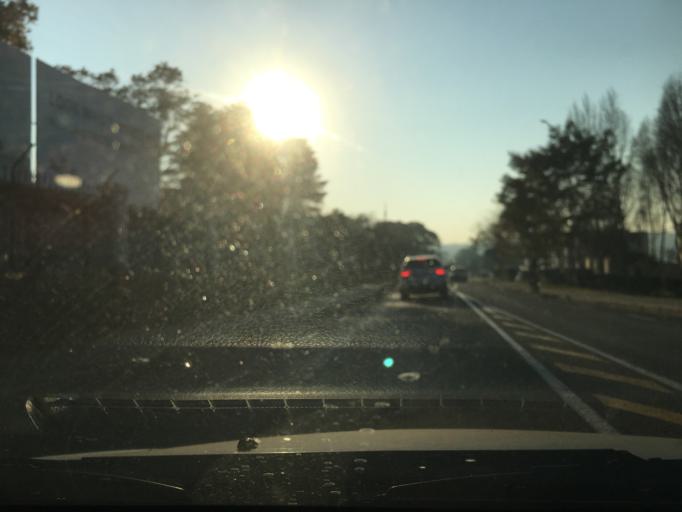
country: ZA
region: Gauteng
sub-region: City of Johannesburg Metropolitan Municipality
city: Johannesburg
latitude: -26.0755
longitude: 28.0289
